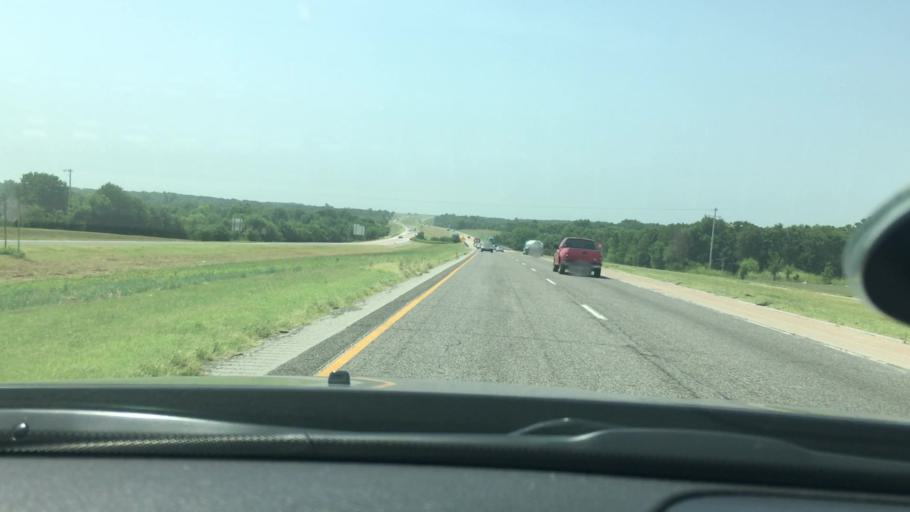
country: US
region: Oklahoma
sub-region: Garvin County
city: Wynnewood
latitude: 34.6501
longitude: -97.2205
